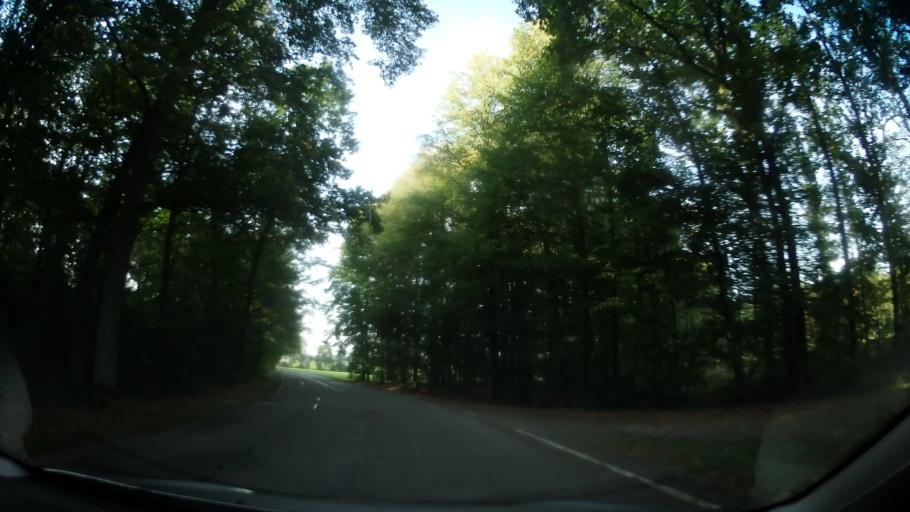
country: CZ
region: Jihocesky
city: Cimelice
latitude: 49.4484
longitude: 14.1469
